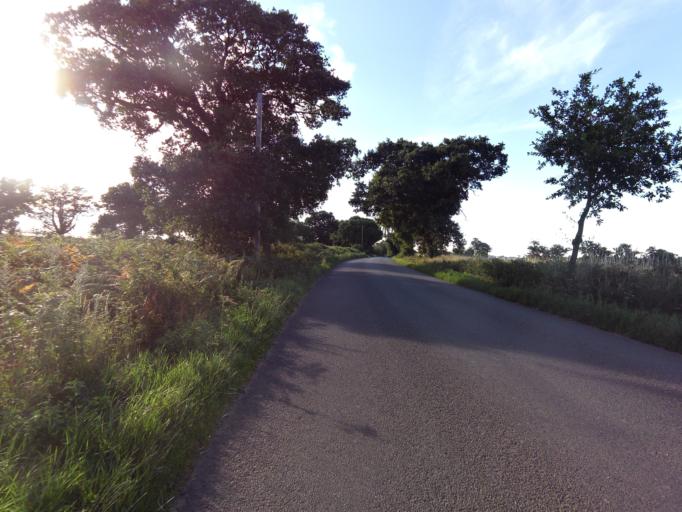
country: GB
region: England
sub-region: Suffolk
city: Kesgrave
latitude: 52.0182
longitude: 1.2184
